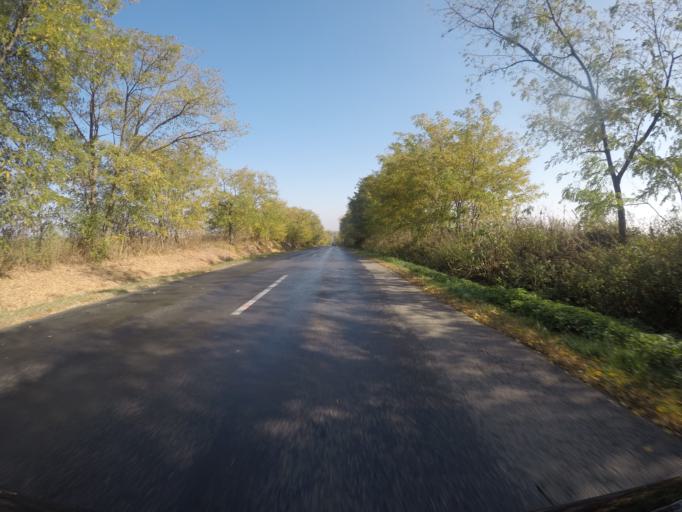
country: HU
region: Tolna
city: Dunaszentgyorgy
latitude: 46.6002
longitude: 18.7743
